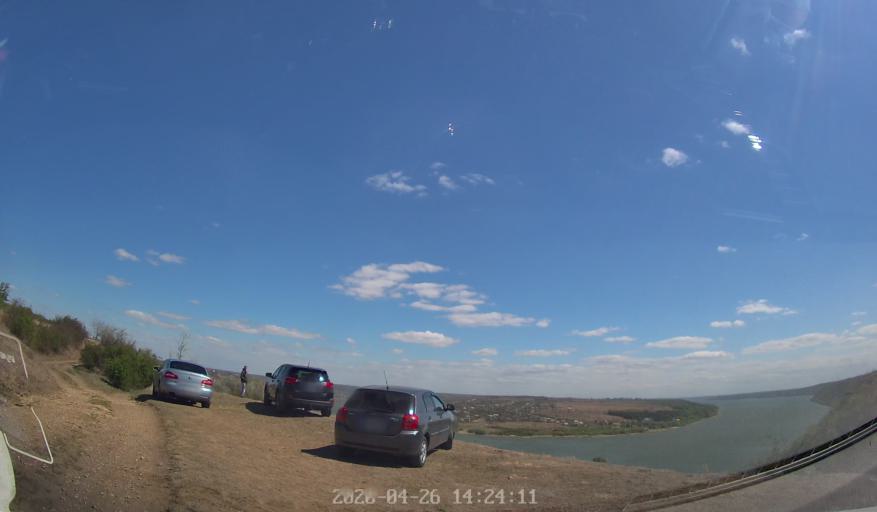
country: MD
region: Telenesti
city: Cocieri
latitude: 47.3594
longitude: 29.0656
